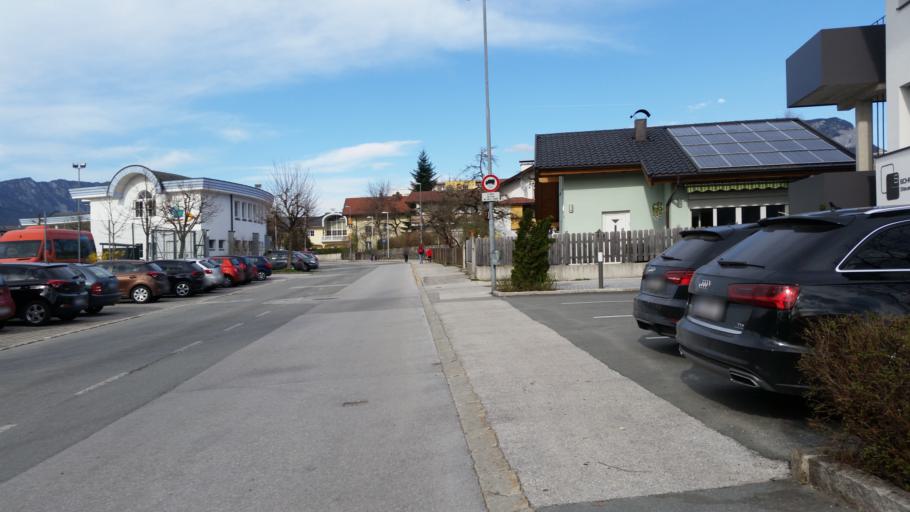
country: AT
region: Tyrol
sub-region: Politischer Bezirk Kufstein
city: Worgl
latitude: 47.4870
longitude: 12.0574
